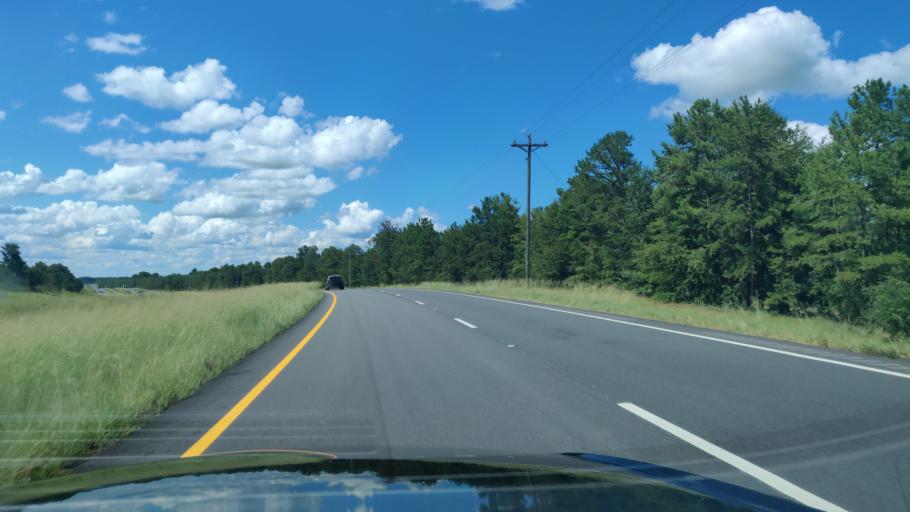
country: US
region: Georgia
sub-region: Stewart County
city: Richland
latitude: 32.1931
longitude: -84.6988
